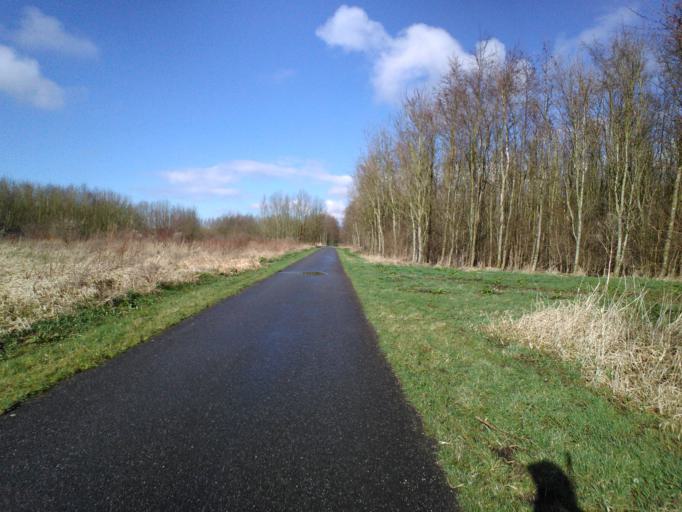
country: NL
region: South Holland
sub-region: Gemeente Delft
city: Delft
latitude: 51.9736
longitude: 4.3785
